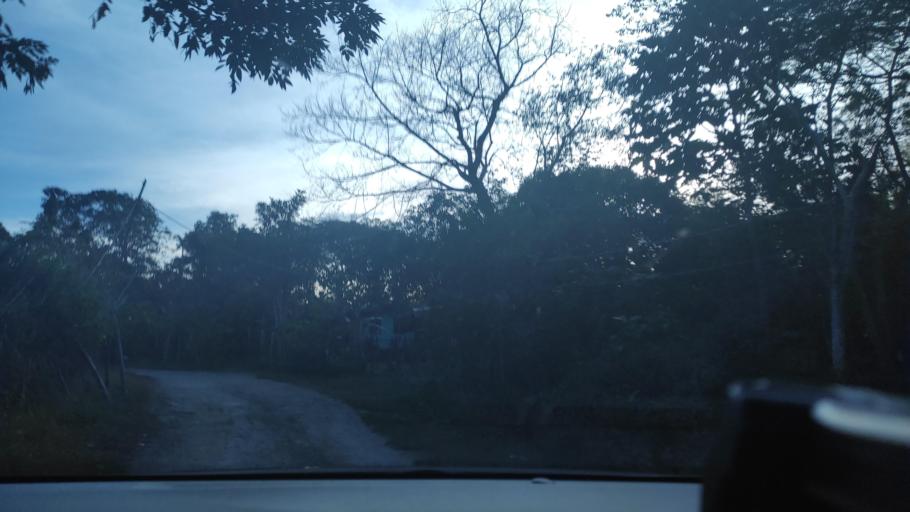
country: PH
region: Ilocos
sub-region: Province of Pangasinan
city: Balingasay
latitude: 16.3092
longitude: 119.8659
